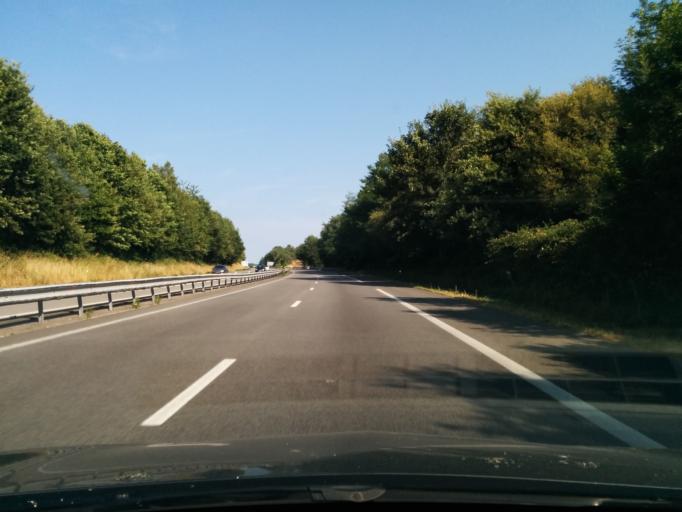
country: FR
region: Limousin
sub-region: Departement de la Haute-Vienne
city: Saint-Germain-les-Belles
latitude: 45.5932
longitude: 1.4550
